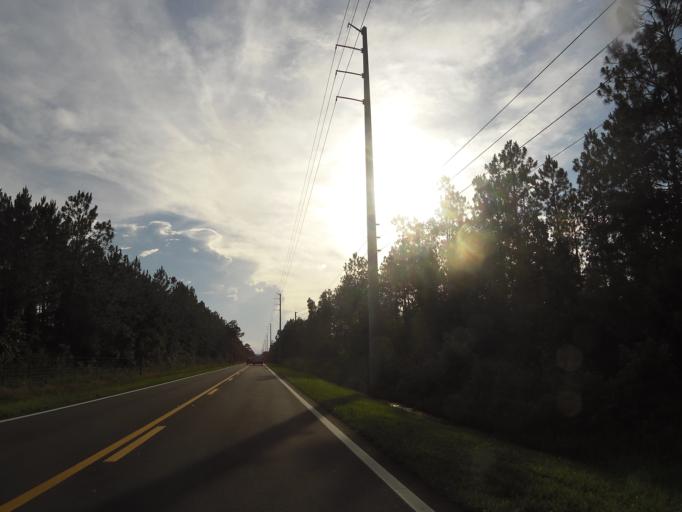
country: US
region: Florida
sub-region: Clay County
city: Green Cove Springs
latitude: 30.0149
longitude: -81.5724
